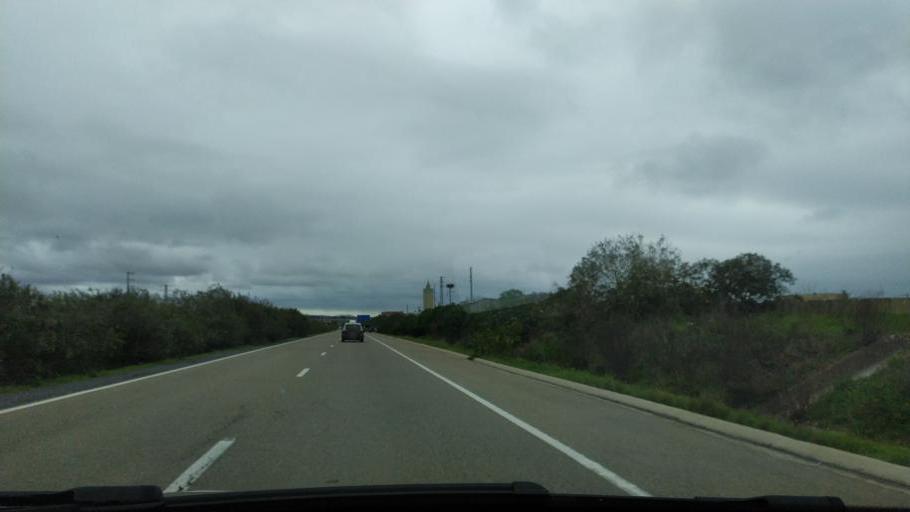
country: MA
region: Gharb-Chrarda-Beni Hssen
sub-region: Kenitra Province
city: Lalla Mimouna
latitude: 34.8672
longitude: -6.2189
